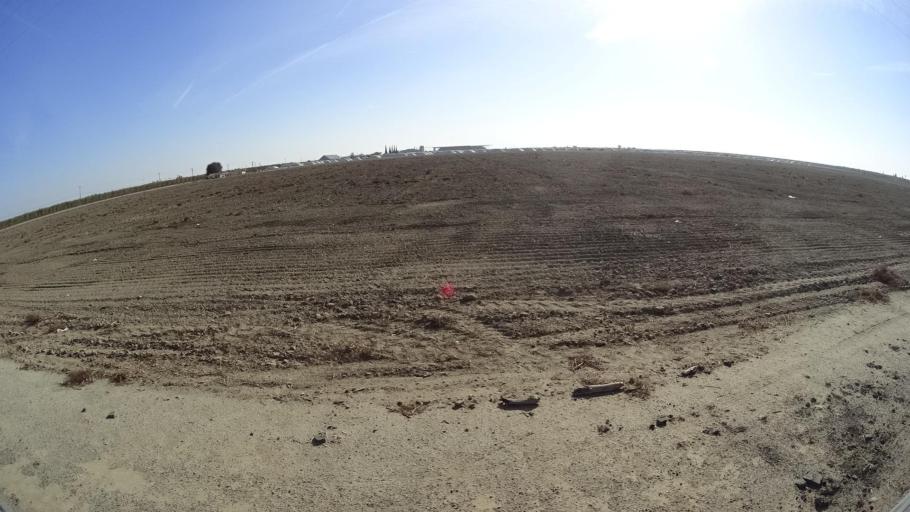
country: US
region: California
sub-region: Kern County
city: McFarland
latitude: 35.7033
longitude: -119.2433
